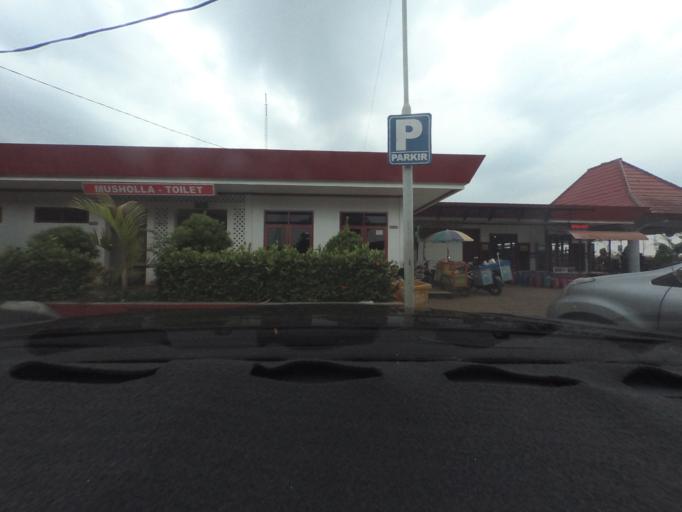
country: ID
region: West Java
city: Gunungkalong
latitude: -6.9538
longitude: 106.7645
